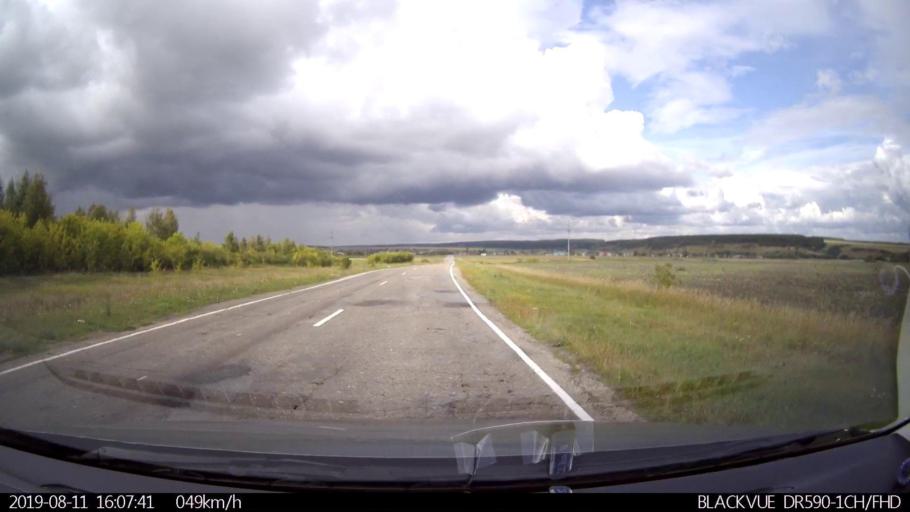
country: RU
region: Ulyanovsk
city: Ignatovka
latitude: 53.9791
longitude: 47.6465
